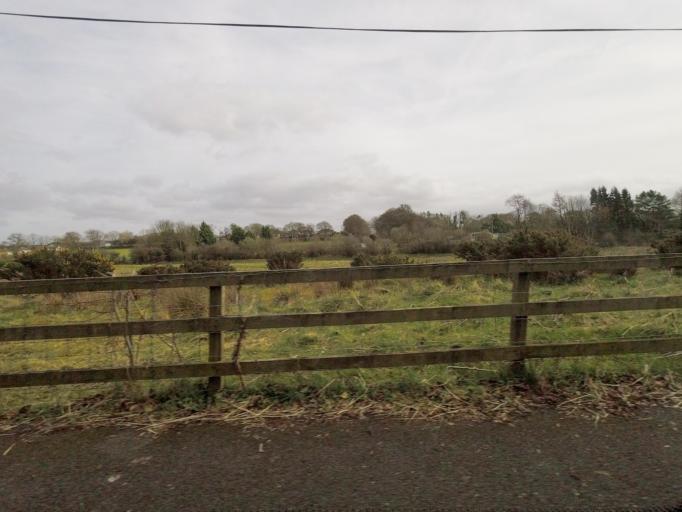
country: IE
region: Leinster
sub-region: Wicklow
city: Blessington
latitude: 53.1637
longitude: -6.5504
